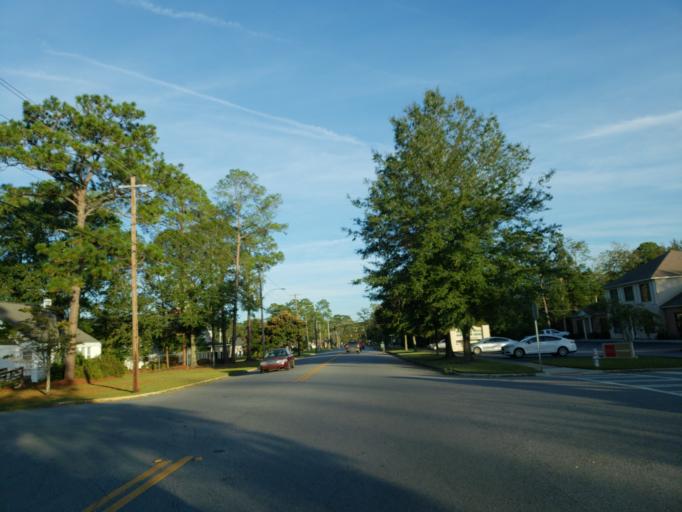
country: US
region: Georgia
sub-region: Tift County
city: Tifton
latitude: 31.4641
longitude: -83.5087
